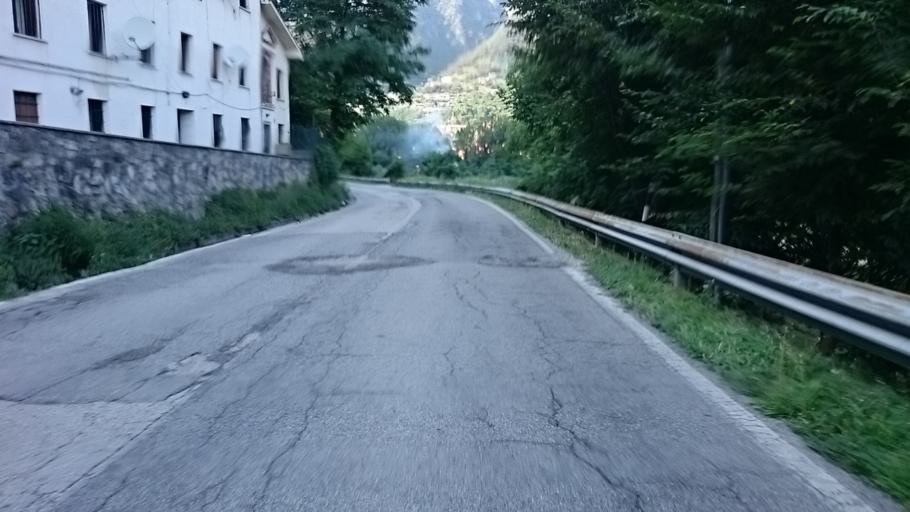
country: IT
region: Veneto
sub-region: Provincia di Vicenza
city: Solagna
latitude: 45.8151
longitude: 11.7144
